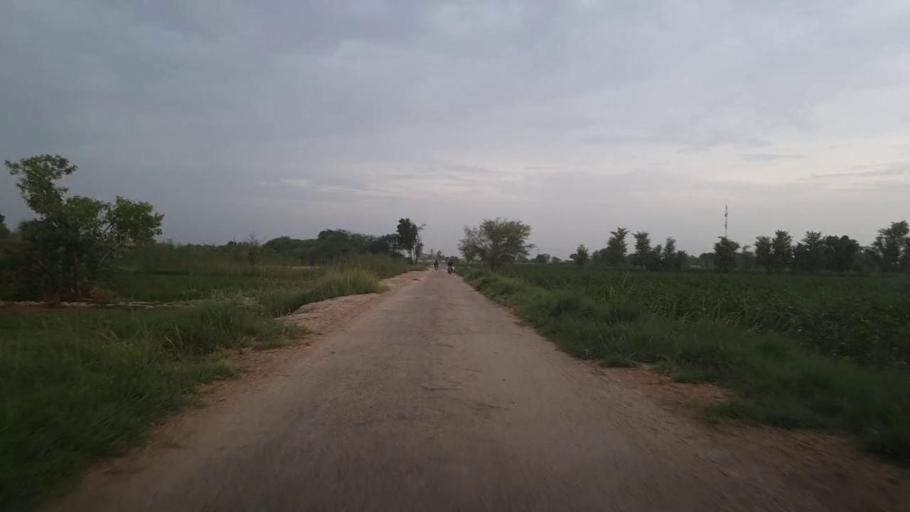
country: PK
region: Sindh
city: Karaundi
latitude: 27.0053
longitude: 68.3435
